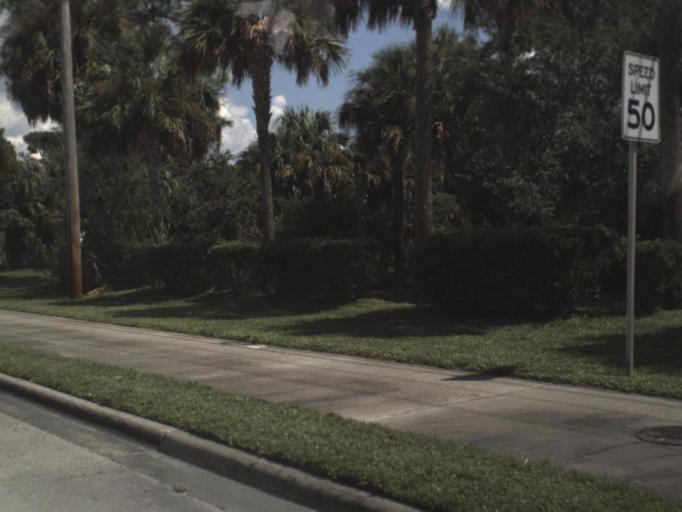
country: US
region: Florida
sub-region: Lee County
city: Suncoast Estates
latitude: 26.6947
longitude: -81.8549
